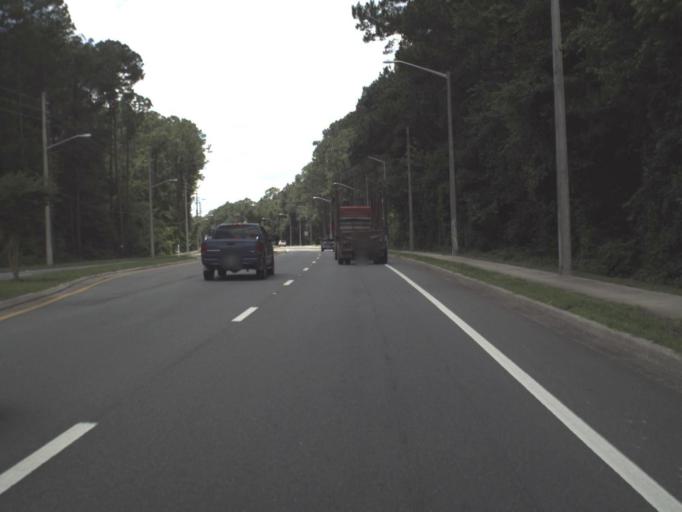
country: US
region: Florida
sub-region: Alachua County
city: Gainesville
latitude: 29.6876
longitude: -82.2948
